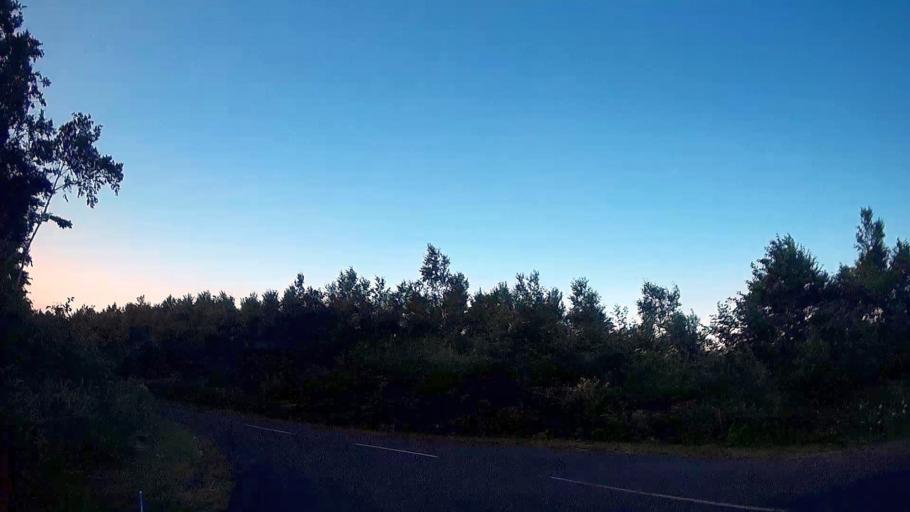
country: JP
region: Hokkaido
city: Iwanai
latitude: 42.6344
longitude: 140.0319
